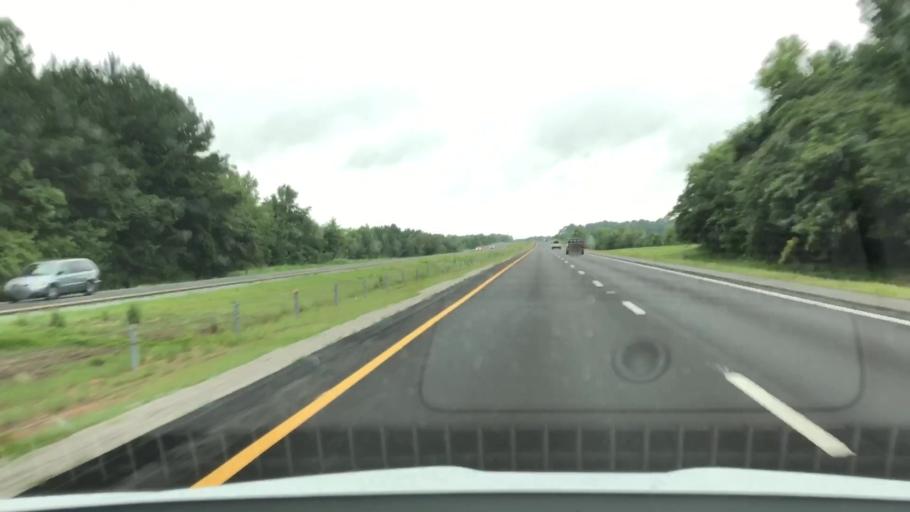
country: US
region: North Carolina
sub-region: Wayne County
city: Goldsboro
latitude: 35.4627
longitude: -77.9857
